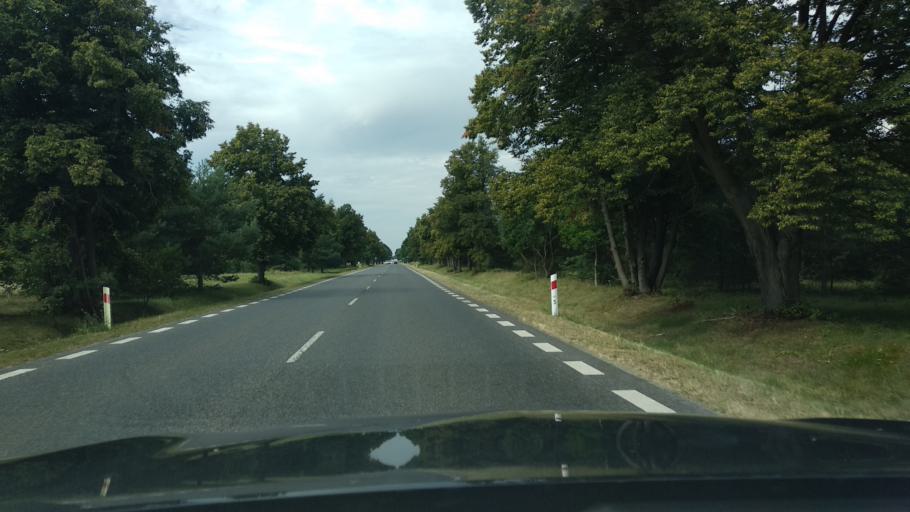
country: PL
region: Masovian Voivodeship
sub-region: Powiat legionowski
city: Serock
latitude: 52.5367
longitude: 21.1041
